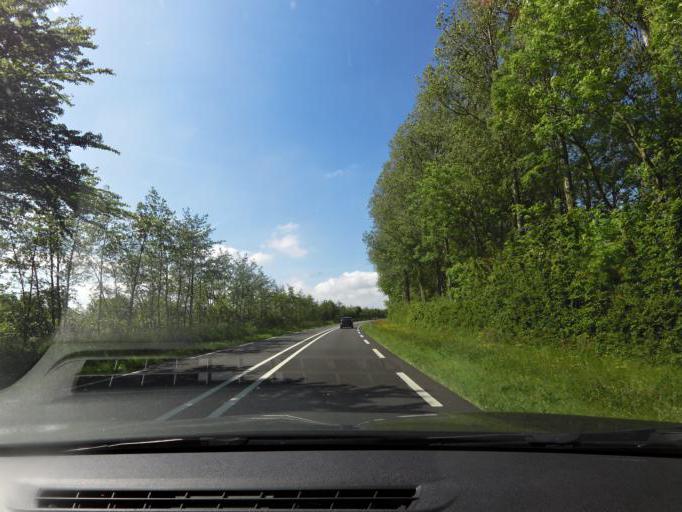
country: NL
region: South Holland
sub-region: Gemeente Hellevoetsluis
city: Nieuw-Helvoet
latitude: 51.8334
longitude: 4.0974
